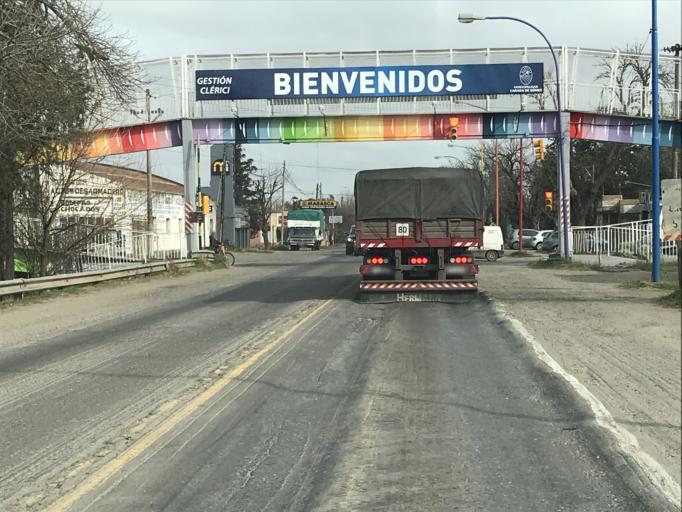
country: AR
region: Santa Fe
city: Canada de Gomez
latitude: -32.8118
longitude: -61.3862
